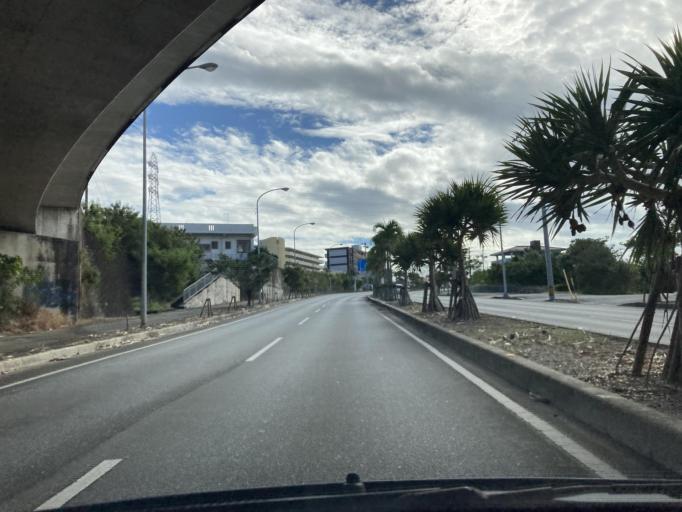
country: JP
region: Okinawa
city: Tomigusuku
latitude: 26.1658
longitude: 127.7254
